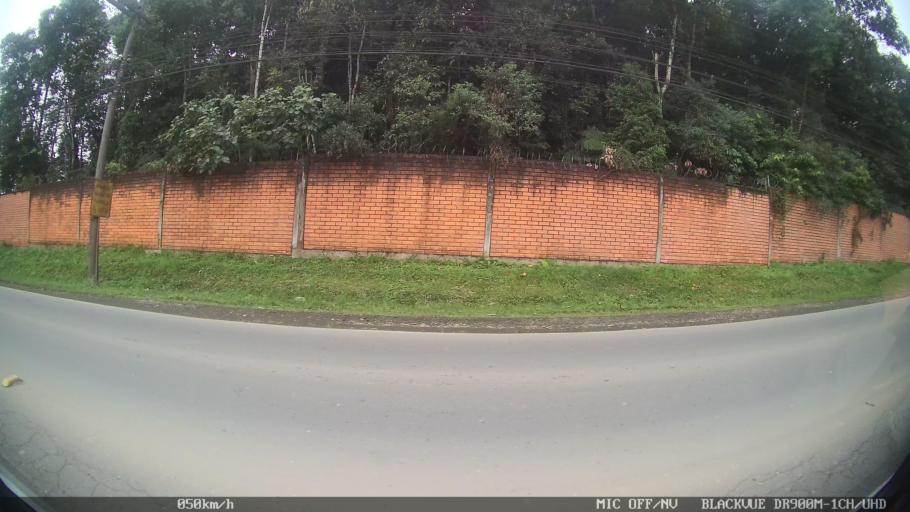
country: BR
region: Santa Catarina
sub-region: Joinville
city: Joinville
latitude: -26.2492
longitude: -48.8769
